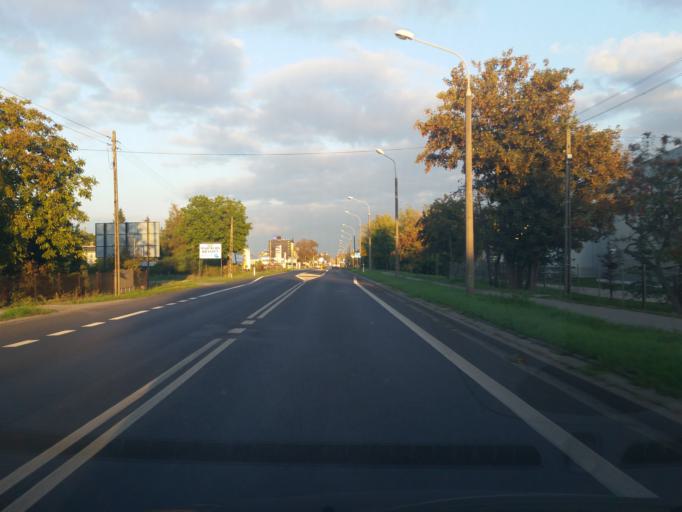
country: PL
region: Masovian Voivodeship
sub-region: Powiat warszawski zachodni
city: Ozarow Mazowiecki
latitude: 52.2110
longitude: 20.7724
